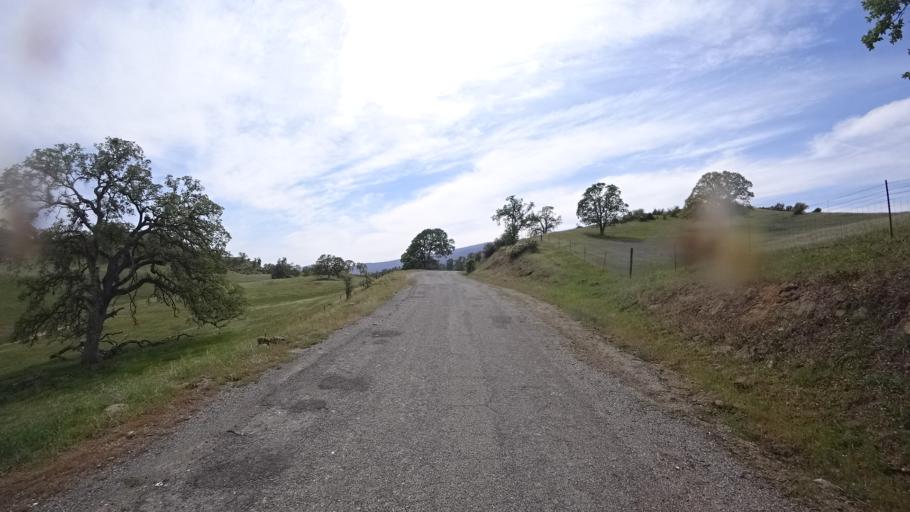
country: US
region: California
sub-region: Glenn County
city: Willows
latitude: 39.6233
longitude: -122.5914
